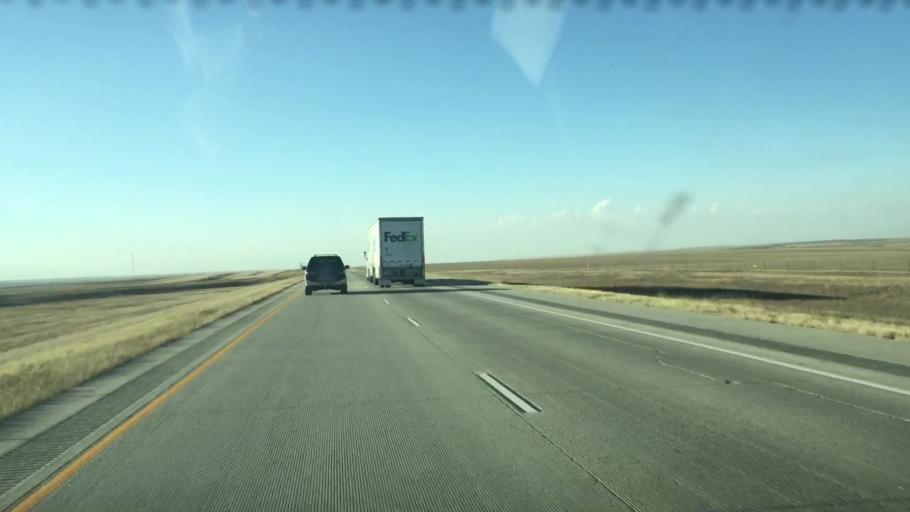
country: US
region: Colorado
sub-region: Lincoln County
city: Limon
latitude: 39.4200
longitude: -103.9080
